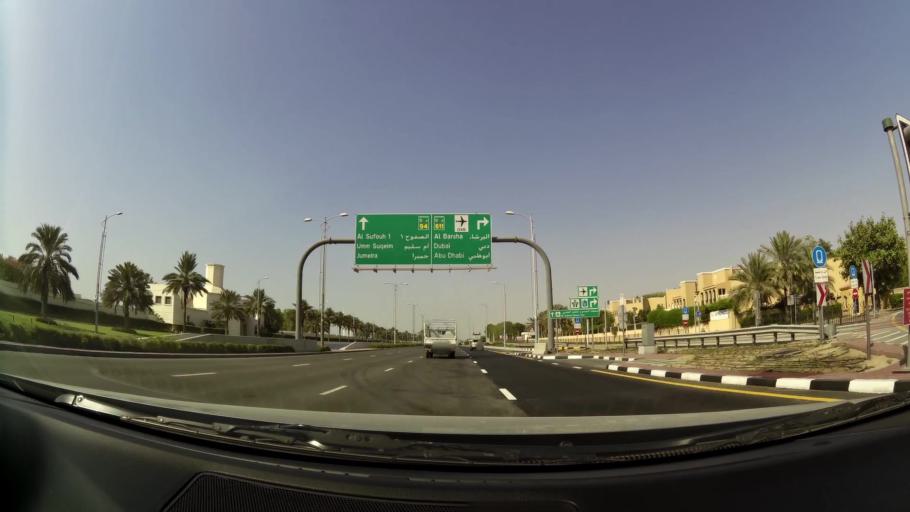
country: AE
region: Dubai
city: Dubai
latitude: 25.1094
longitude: 55.1663
